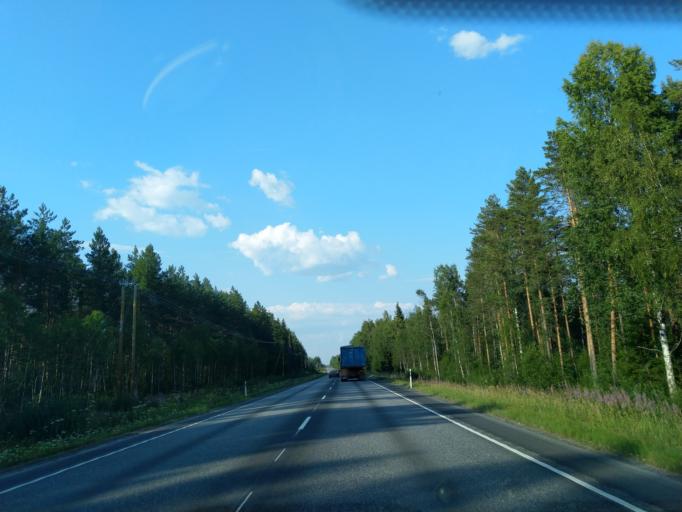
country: FI
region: Satakunta
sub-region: Pori
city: Pomarkku
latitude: 61.7116
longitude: 22.0368
